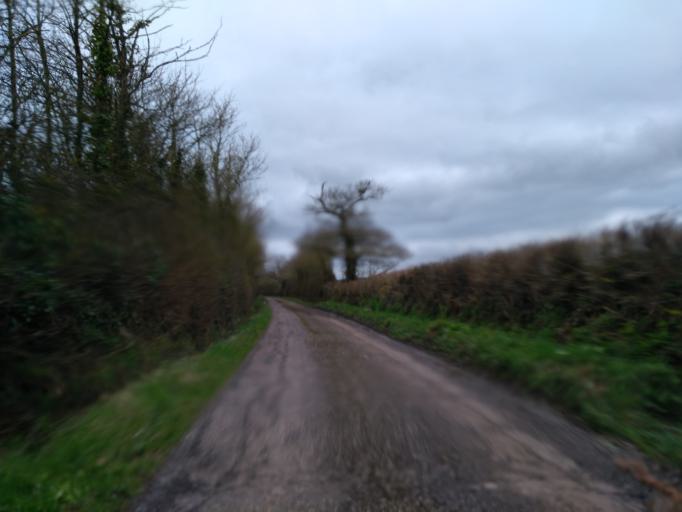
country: GB
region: England
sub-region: Devon
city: Heavitree
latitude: 50.7968
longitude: -3.5003
